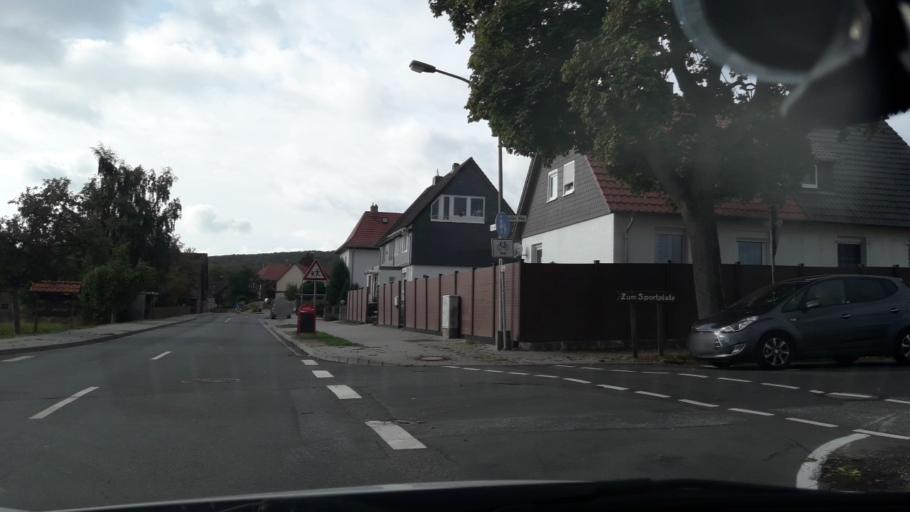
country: DE
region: Lower Saxony
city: Liebenburg
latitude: 52.0013
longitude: 10.4414
